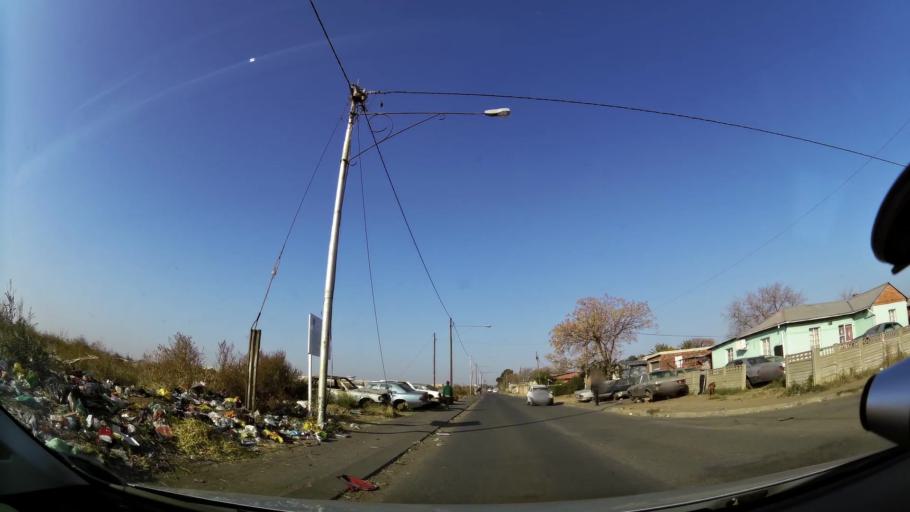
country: ZA
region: Orange Free State
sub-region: Mangaung Metropolitan Municipality
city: Bloemfontein
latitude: -29.1363
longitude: 26.2522
